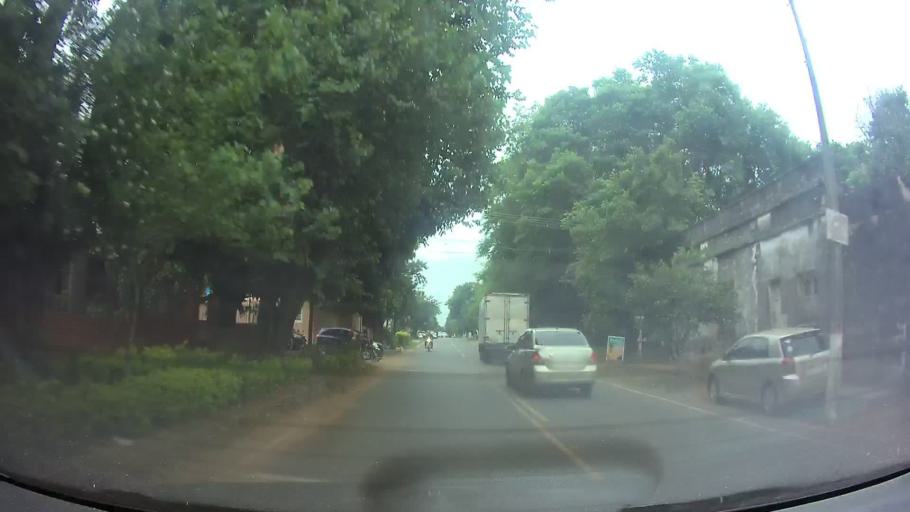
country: PY
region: Paraguari
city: Carapegua
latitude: -25.7690
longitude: -57.2467
